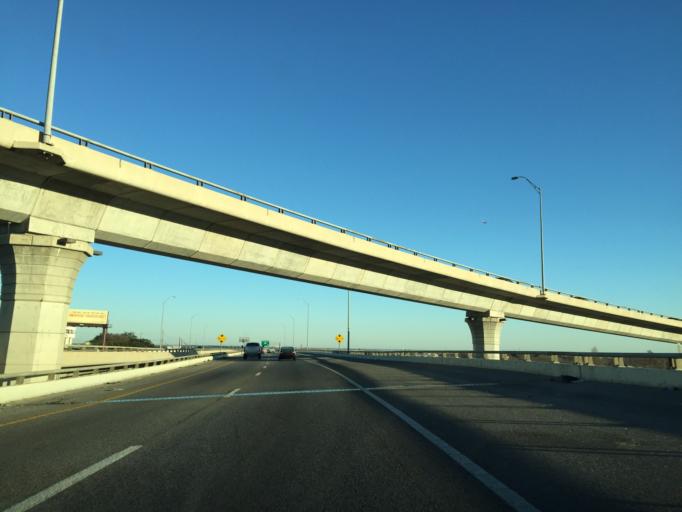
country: US
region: Texas
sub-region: Travis County
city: Austin
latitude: 30.3395
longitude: -97.7009
